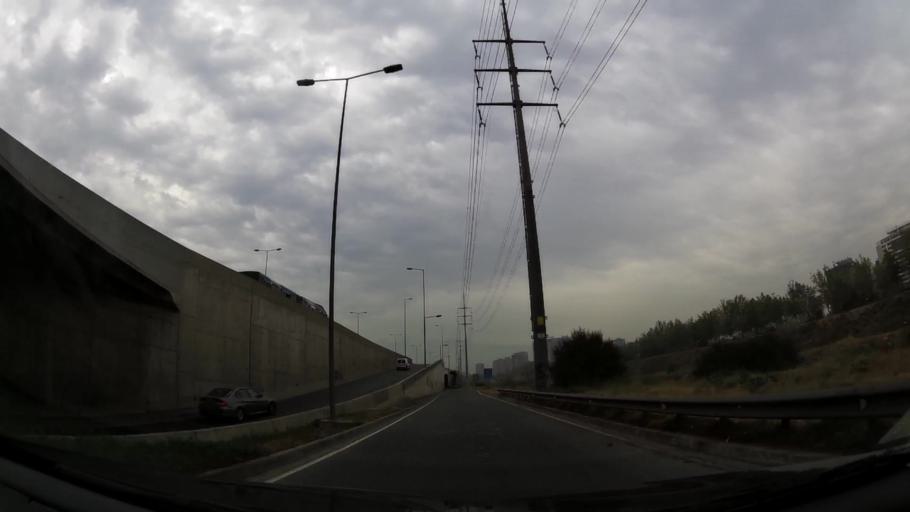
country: CL
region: Santiago Metropolitan
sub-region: Provincia de Santiago
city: Santiago
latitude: -33.4277
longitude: -70.6672
